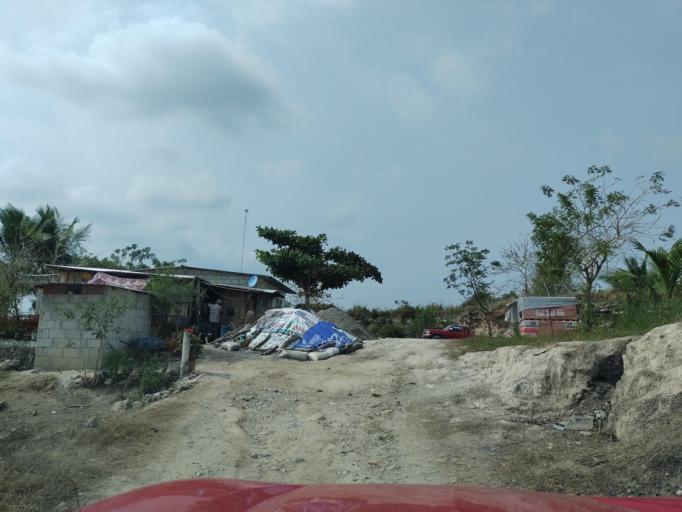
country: MX
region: Veracruz
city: Agua Dulce
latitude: 20.3619
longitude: -97.2980
